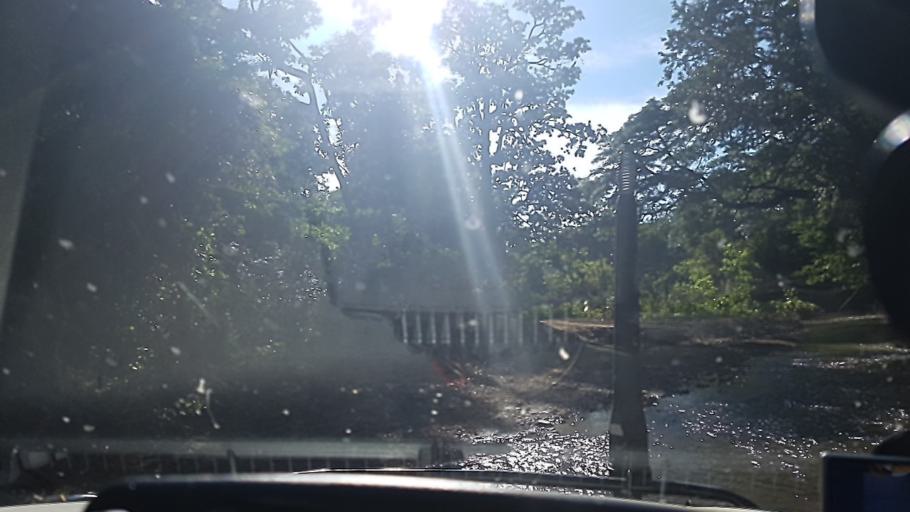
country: NI
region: Rivas
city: Tola
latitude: 11.5382
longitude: -86.1271
